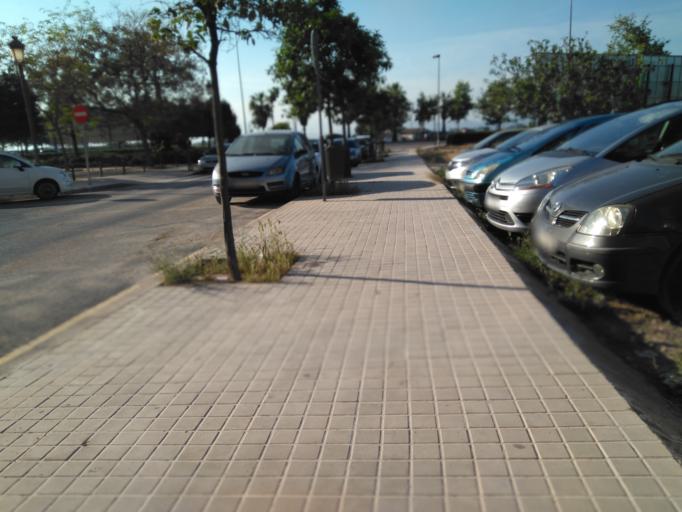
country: ES
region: Valencia
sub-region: Provincia de Valencia
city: Tavernes Blanques
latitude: 39.4986
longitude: -0.3764
